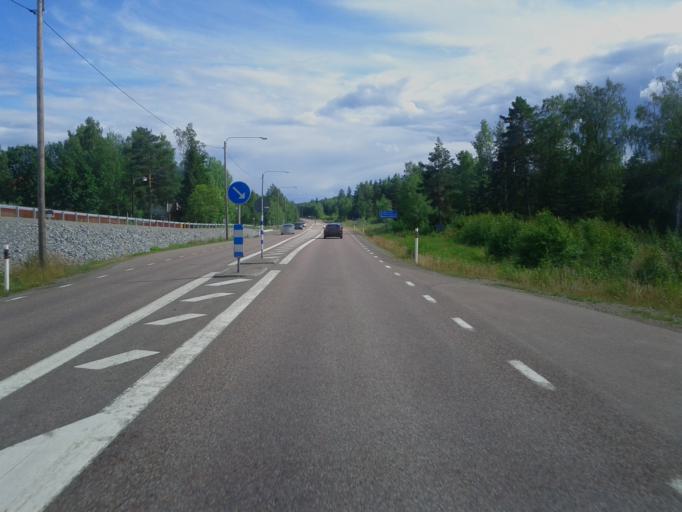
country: SE
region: Dalarna
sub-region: Faluns Kommun
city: Grycksbo
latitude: 60.6654
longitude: 15.5450
